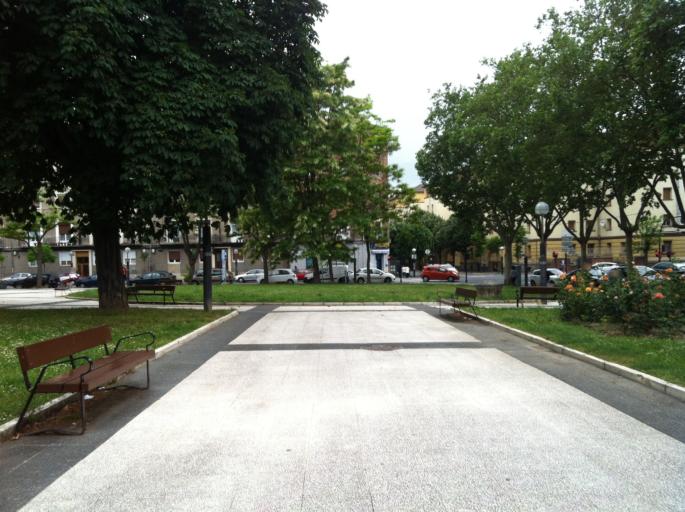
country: ES
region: Basque Country
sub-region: Provincia de Alava
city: Gasteiz / Vitoria
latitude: 42.8382
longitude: -2.6679
